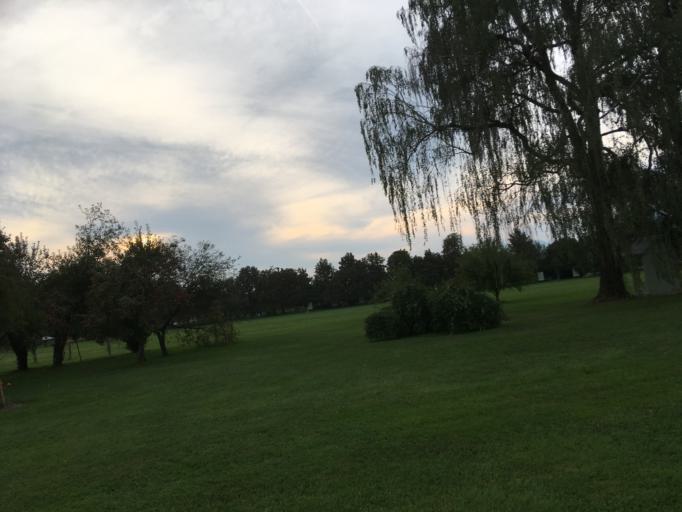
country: SI
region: Domzale
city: Radomlje
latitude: 46.1849
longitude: 14.6098
